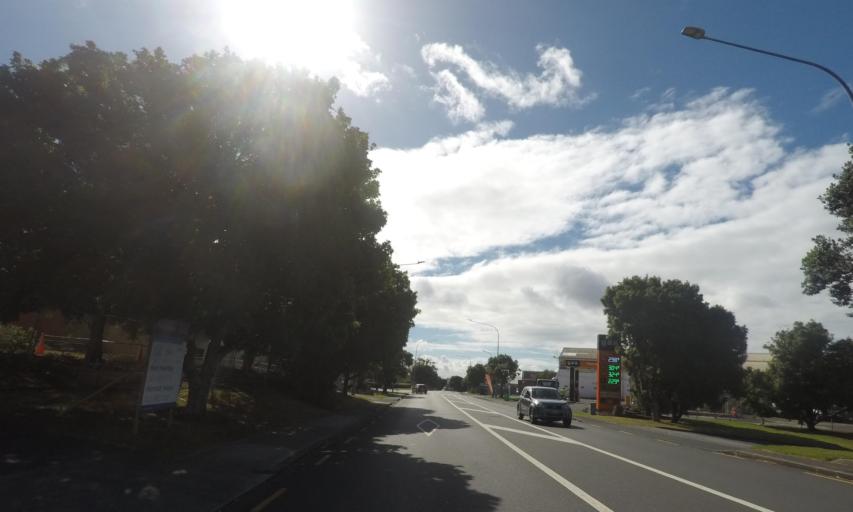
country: NZ
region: Auckland
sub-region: Auckland
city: Tamaki
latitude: -36.9229
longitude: 174.8514
